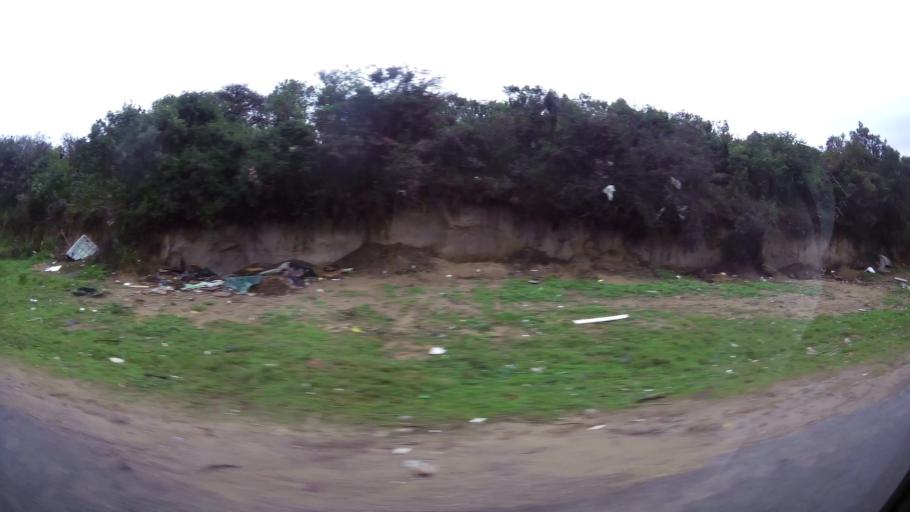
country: ZA
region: Eastern Cape
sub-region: Nelson Mandela Bay Metropolitan Municipality
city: Port Elizabeth
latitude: -33.9990
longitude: 25.5767
